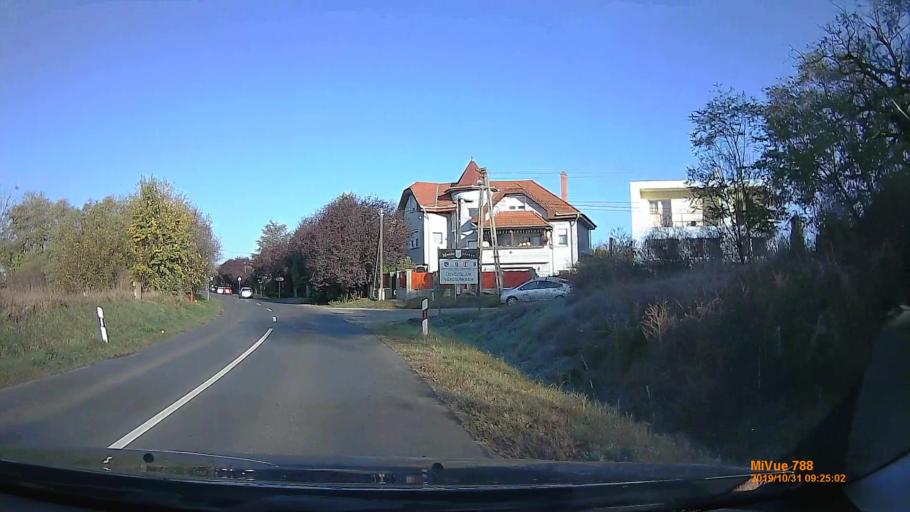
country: HU
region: Pest
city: Maglod
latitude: 47.4395
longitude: 19.3742
